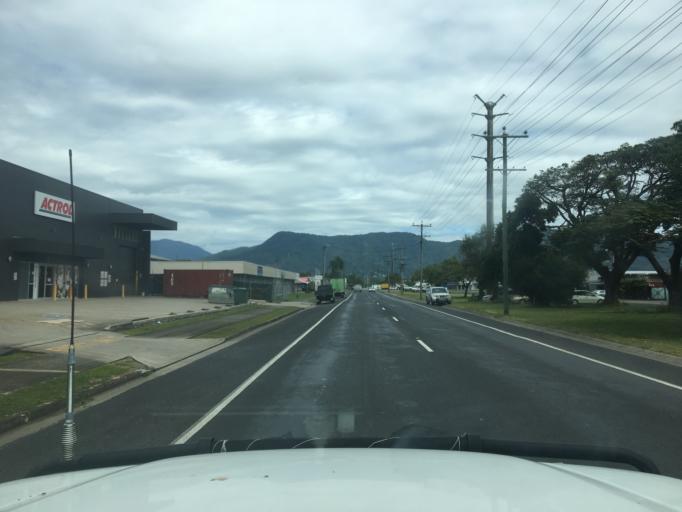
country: AU
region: Queensland
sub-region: Cairns
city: Woree
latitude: -16.9396
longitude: 145.7618
